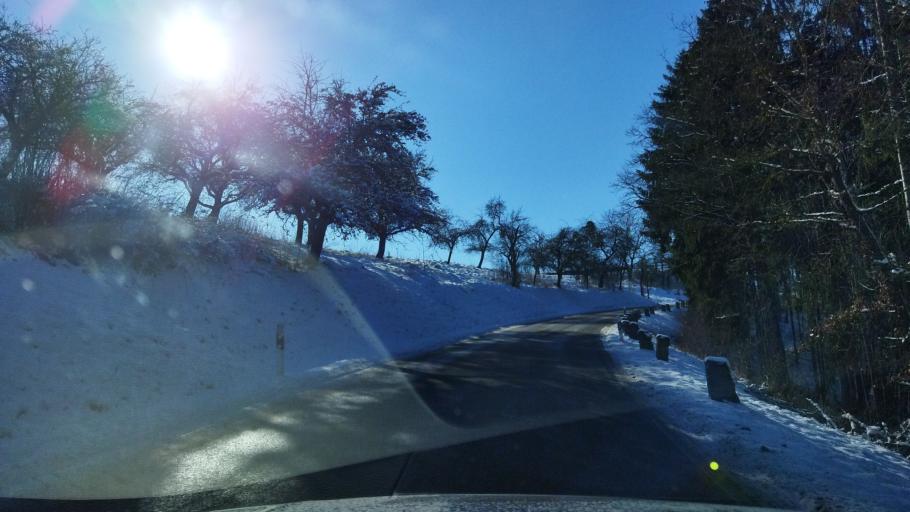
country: DE
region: Baden-Wuerttemberg
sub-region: Regierungsbezirk Stuttgart
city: Ilshofen
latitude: 49.2069
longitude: 9.9219
